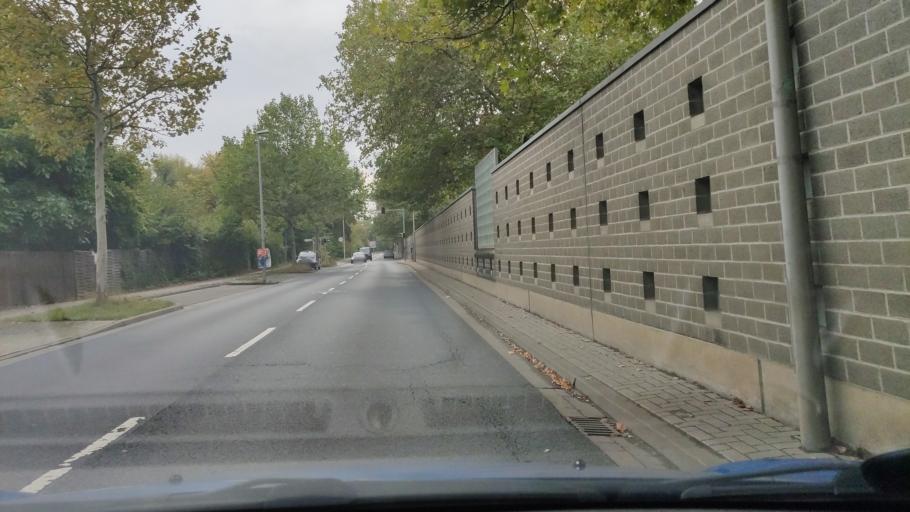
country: DE
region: Lower Saxony
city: Ronnenberg
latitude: 52.3527
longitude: 9.6756
